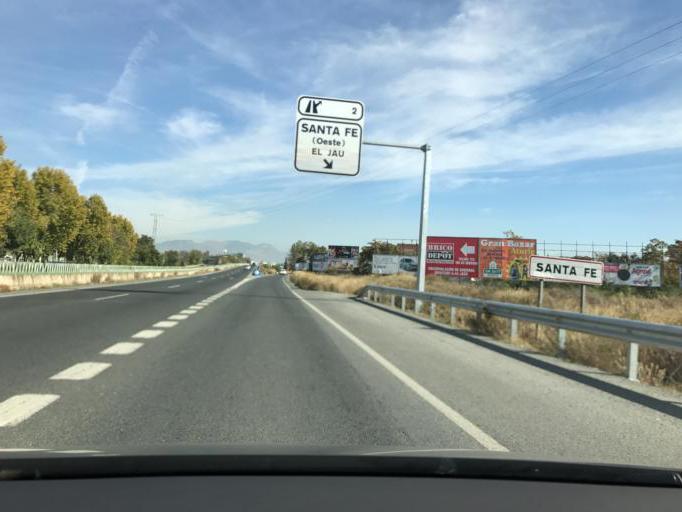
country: ES
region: Andalusia
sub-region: Provincia de Granada
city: Chauchina
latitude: 37.1906
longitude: -3.7295
